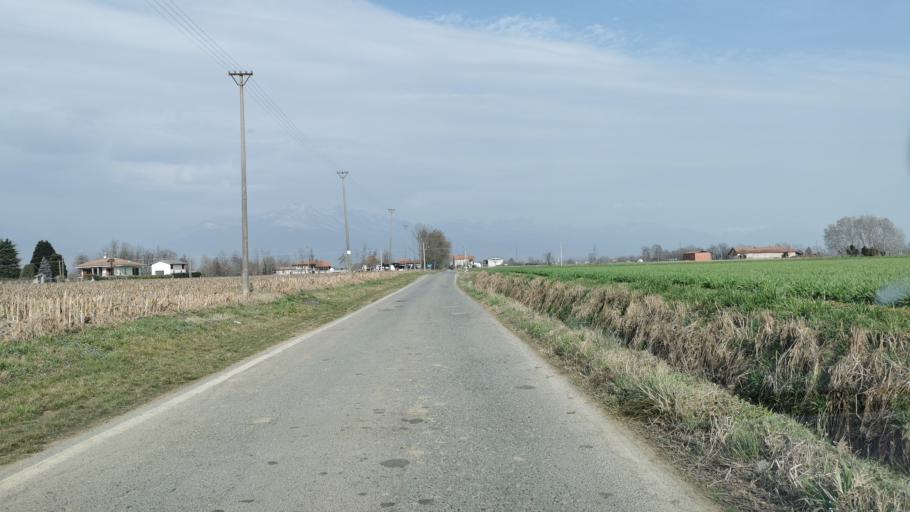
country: IT
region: Piedmont
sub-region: Provincia di Torino
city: Front
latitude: 45.2922
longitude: 7.6881
